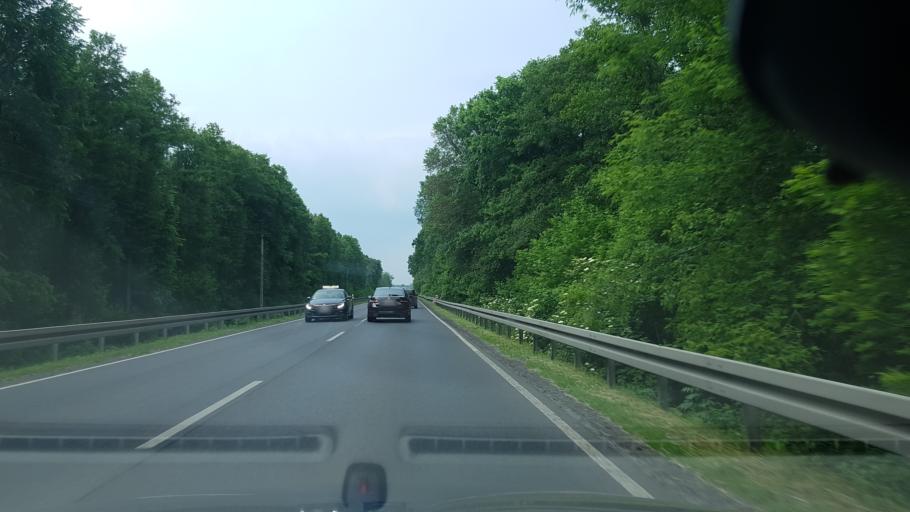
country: PL
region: Masovian Voivodeship
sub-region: Powiat legionowski
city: Wieliszew
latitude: 52.4385
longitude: 20.9933
